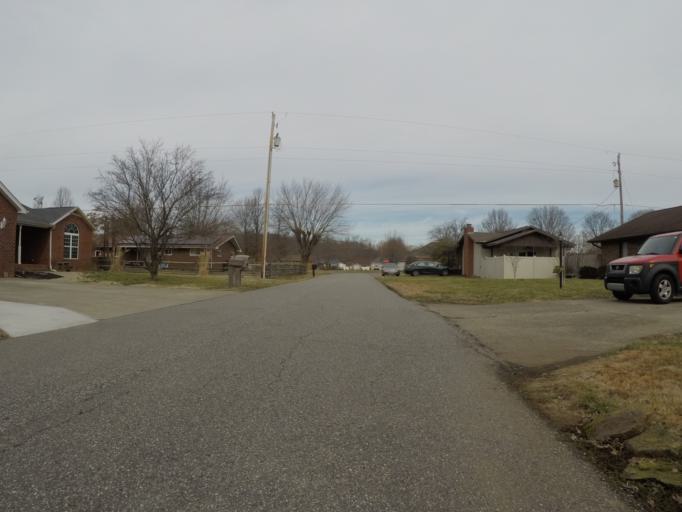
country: US
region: West Virginia
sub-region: Cabell County
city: Pea Ridge
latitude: 38.4495
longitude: -82.3515
